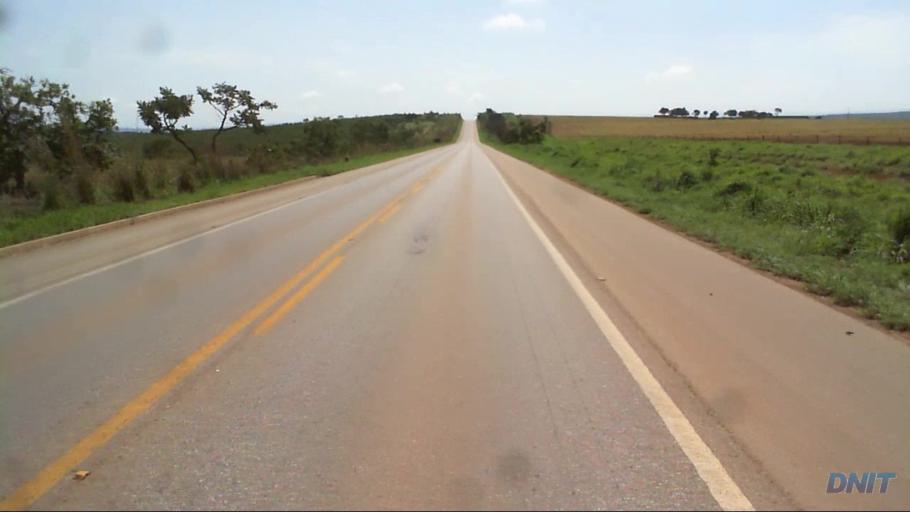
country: BR
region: Goias
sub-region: Barro Alto
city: Barro Alto
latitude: -15.2064
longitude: -48.7187
